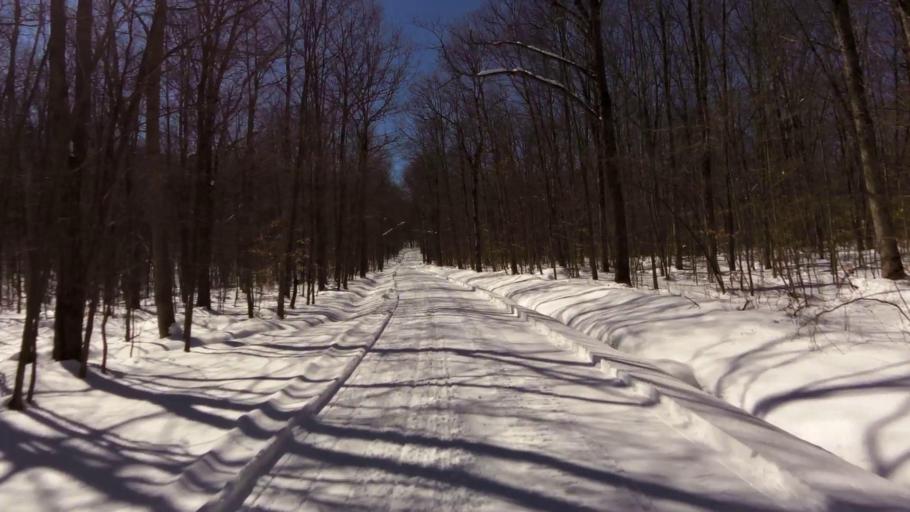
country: US
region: New York
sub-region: Allegany County
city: Houghton
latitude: 42.3456
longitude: -78.1982
